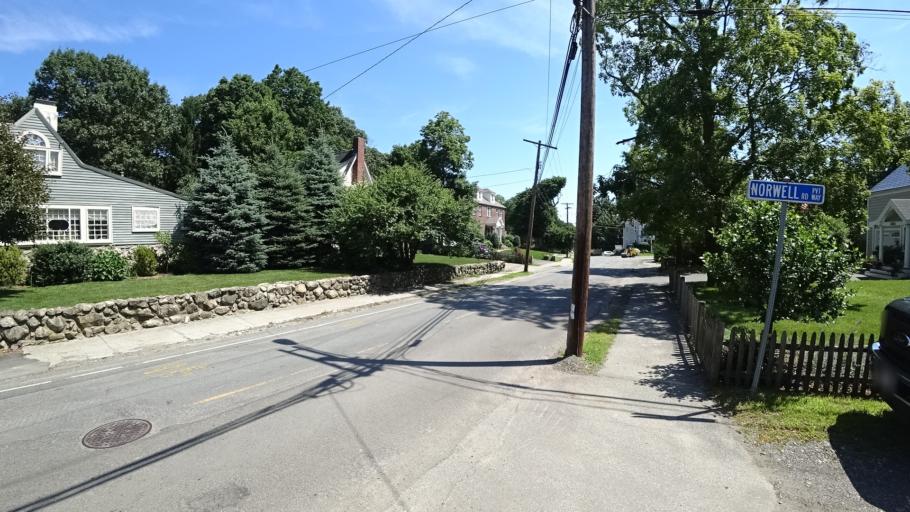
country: US
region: Massachusetts
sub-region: Norfolk County
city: Dedham
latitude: 42.2423
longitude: -71.1587
